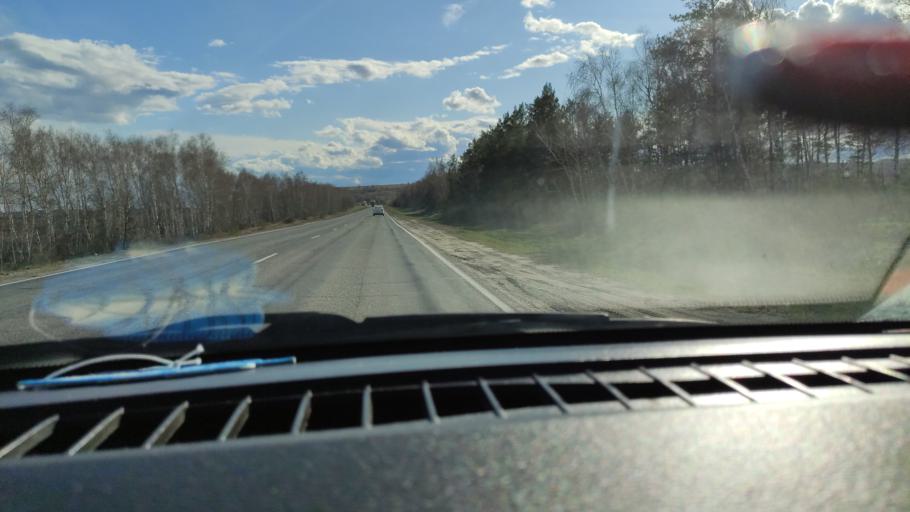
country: RU
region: Saratov
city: Sennoy
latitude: 52.1037
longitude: 46.8182
